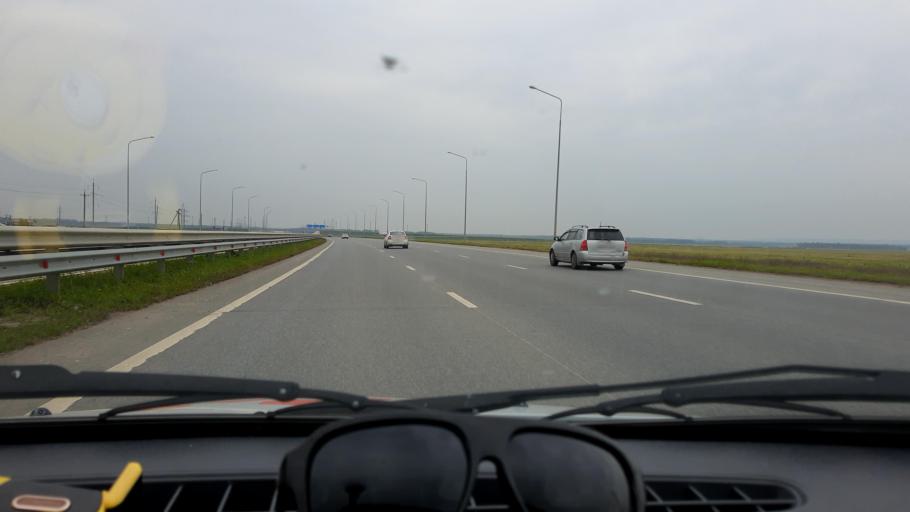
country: RU
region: Bashkortostan
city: Mikhaylovka
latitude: 54.8747
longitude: 55.7274
